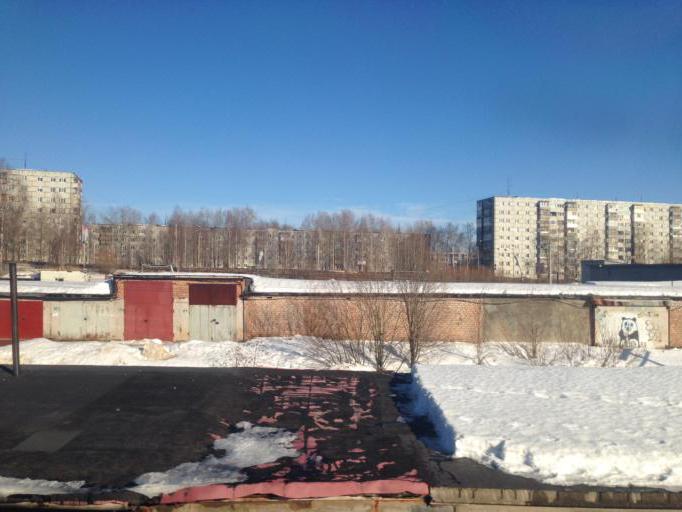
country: RU
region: Komi Republic
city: Ezhva
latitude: 61.7906
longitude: 50.7390
